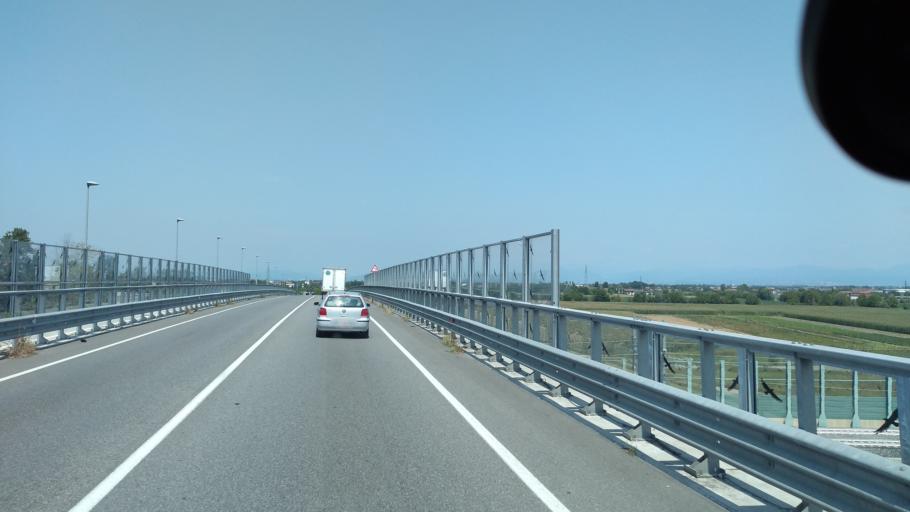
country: IT
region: Lombardy
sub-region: Provincia di Bergamo
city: Calvenzano
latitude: 45.5067
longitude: 9.6193
